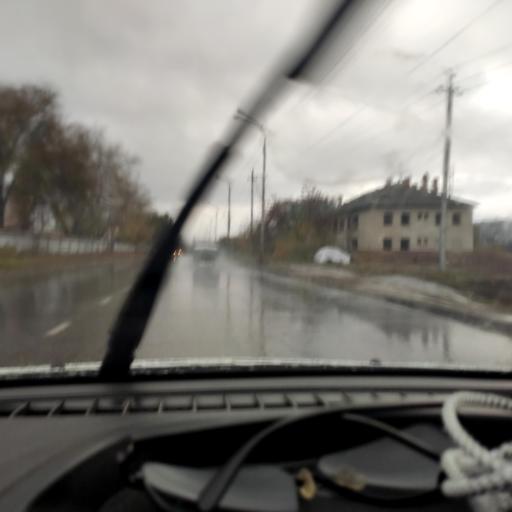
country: RU
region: Samara
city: Zhigulevsk
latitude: 53.4744
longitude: 49.5345
